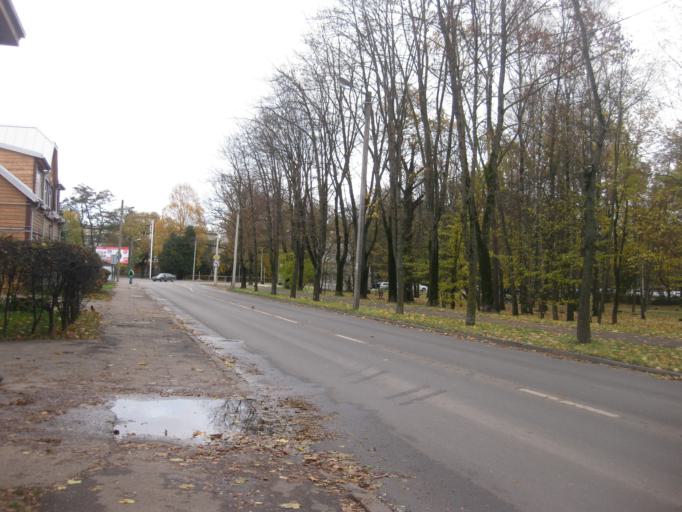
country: LT
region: Kauno apskritis
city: Dainava (Kaunas)
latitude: 54.9037
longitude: 23.9475
